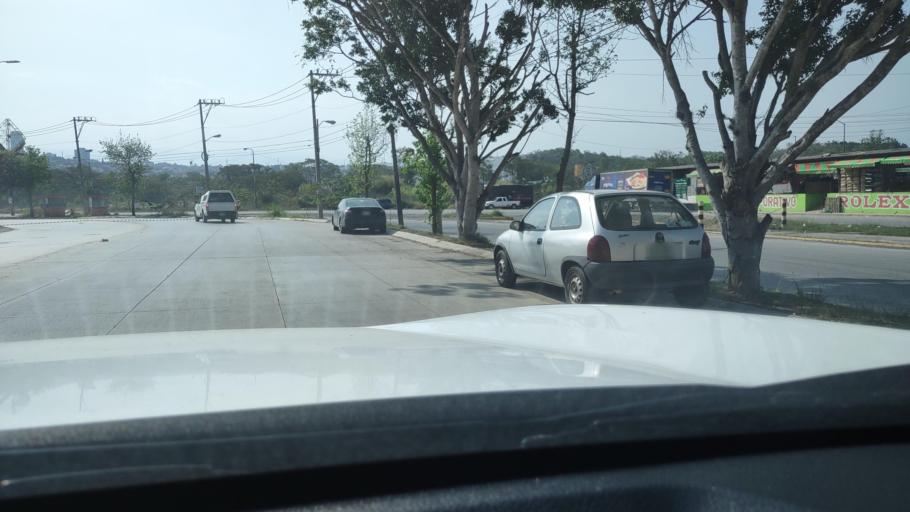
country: MX
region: Veracruz
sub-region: Emiliano Zapata
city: Las Trancas
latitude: 19.5140
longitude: -96.8561
